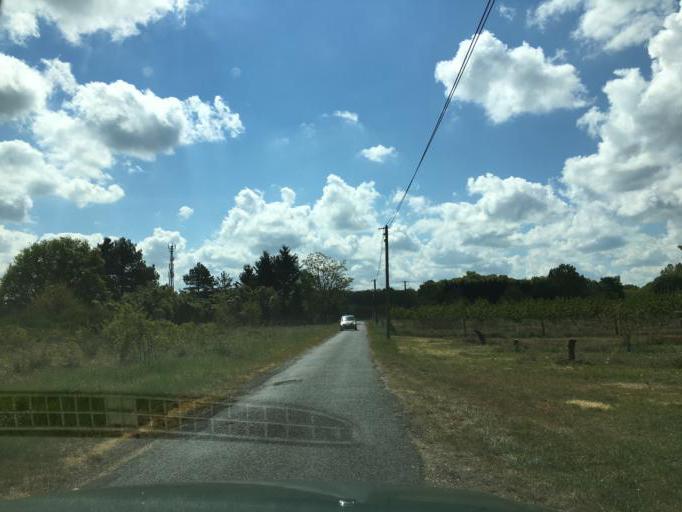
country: FR
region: Centre
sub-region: Departement du Loiret
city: Saint-Pryve-Saint-Mesmin
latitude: 47.8616
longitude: 1.8604
